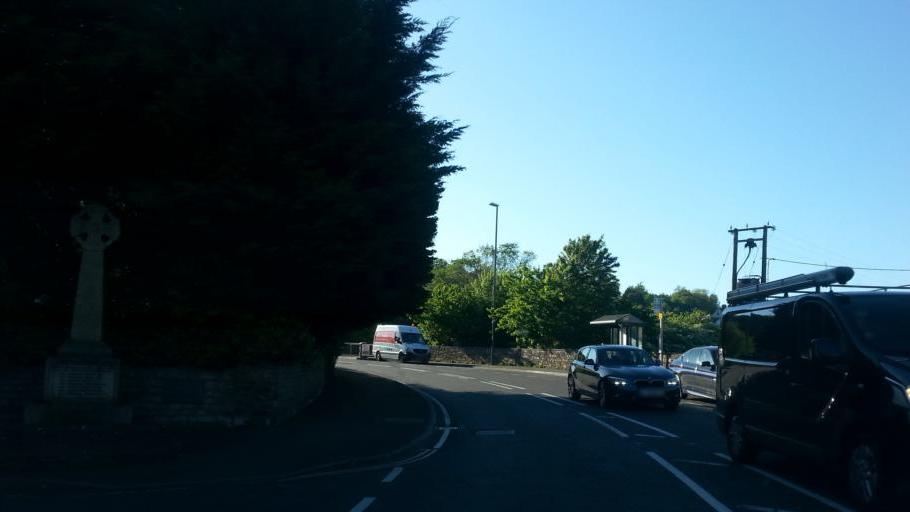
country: GB
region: England
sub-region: Bath and North East Somerset
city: Publow
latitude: 51.3713
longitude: -2.5483
